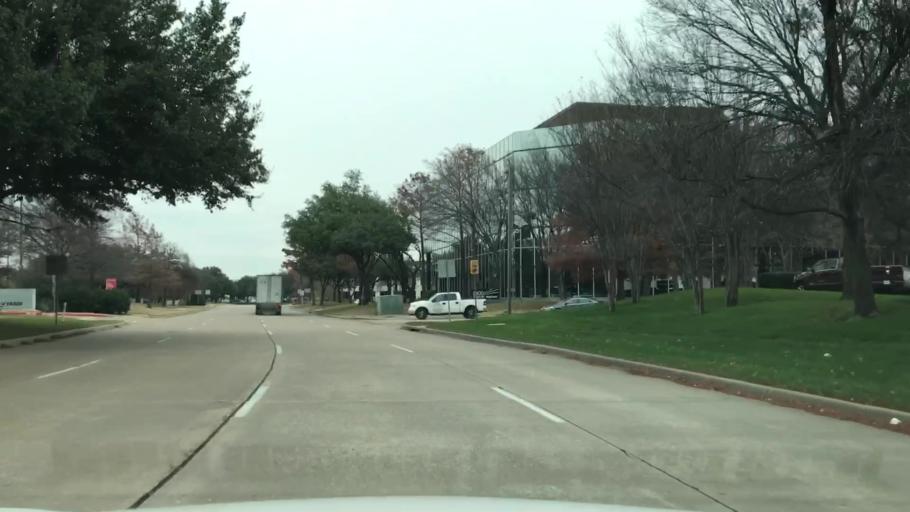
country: US
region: Texas
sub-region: Dallas County
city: Coppell
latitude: 32.9241
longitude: -97.0153
